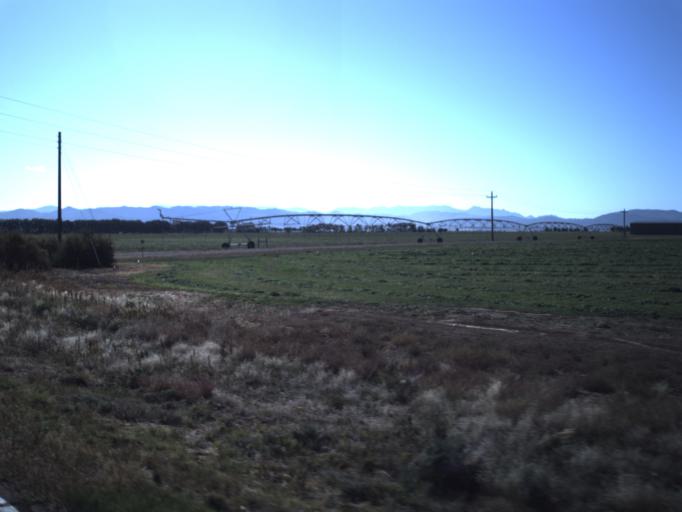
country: US
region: Utah
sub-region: Washington County
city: Enterprise
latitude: 37.7262
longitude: -113.7027
